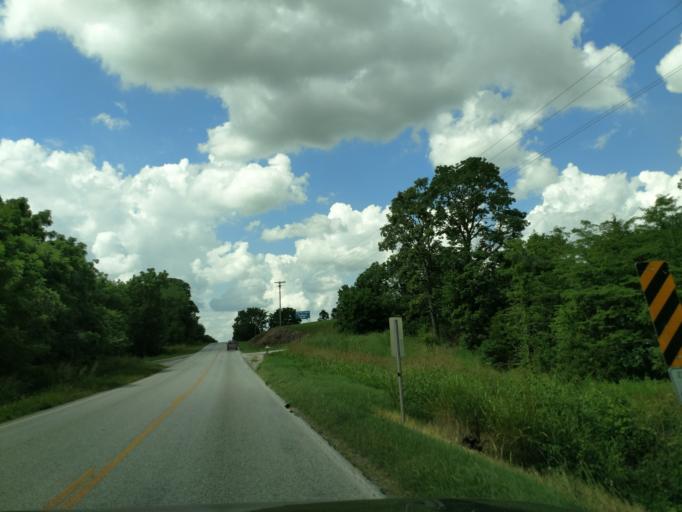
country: US
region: Arkansas
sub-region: Carroll County
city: Berryville
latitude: 36.4009
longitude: -93.5660
